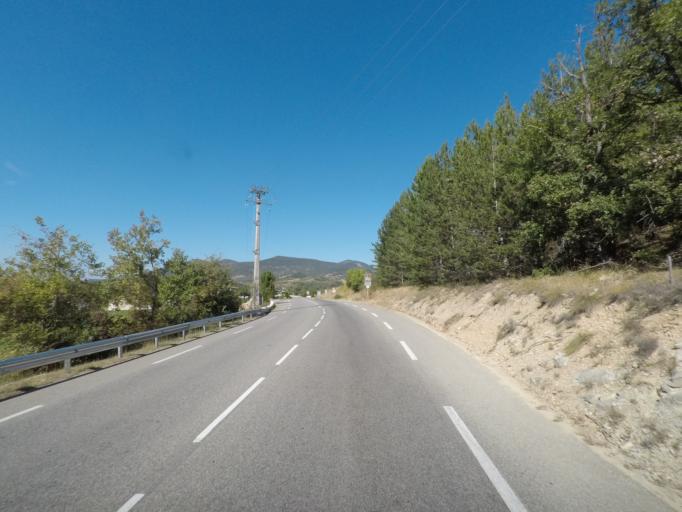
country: FR
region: Rhone-Alpes
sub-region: Departement de la Drome
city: Aouste-sur-Sye
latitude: 44.6913
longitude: 5.2076
